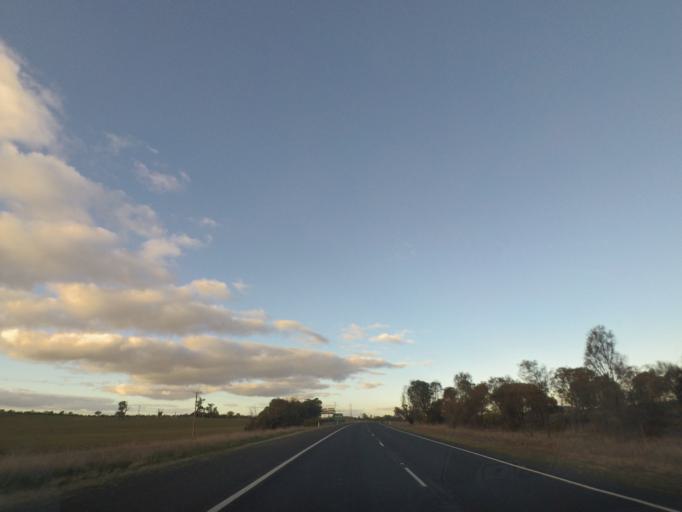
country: AU
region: New South Wales
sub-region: Yass Valley
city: Yass
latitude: -34.7669
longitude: 148.7552
